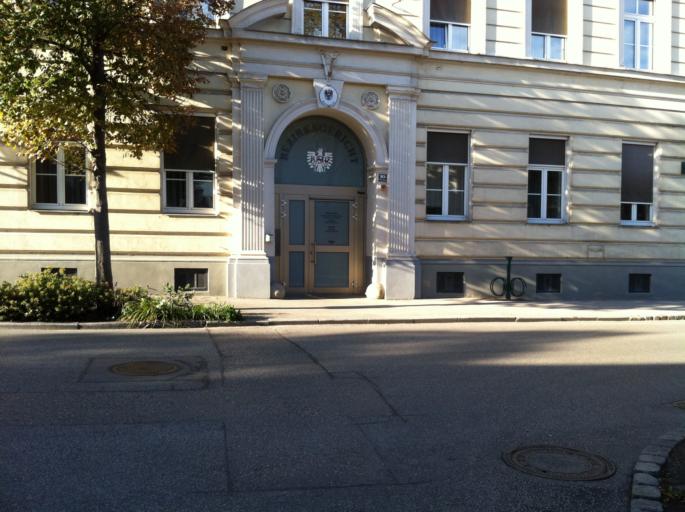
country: AT
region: Lower Austria
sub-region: Politischer Bezirk Tulln
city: Tulln
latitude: 48.3325
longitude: 16.0530
